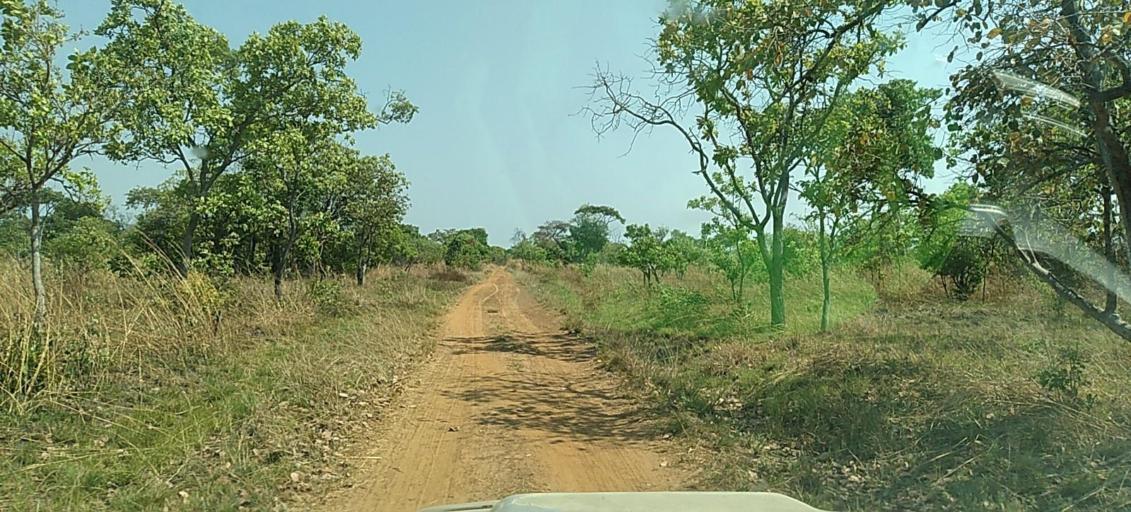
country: ZM
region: North-Western
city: Kalengwa
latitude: -13.2481
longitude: 24.7605
